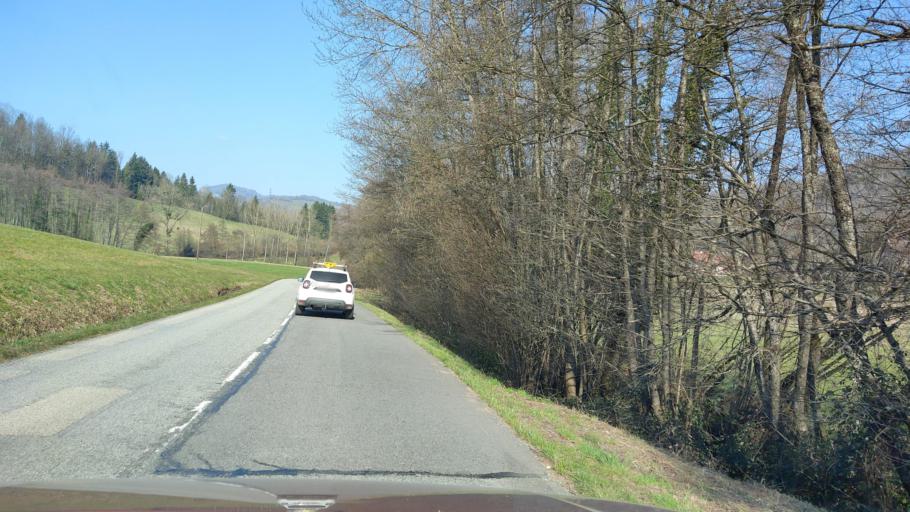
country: FR
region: Rhone-Alpes
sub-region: Departement de la Savoie
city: La Bridoire
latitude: 45.5132
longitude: 5.7371
